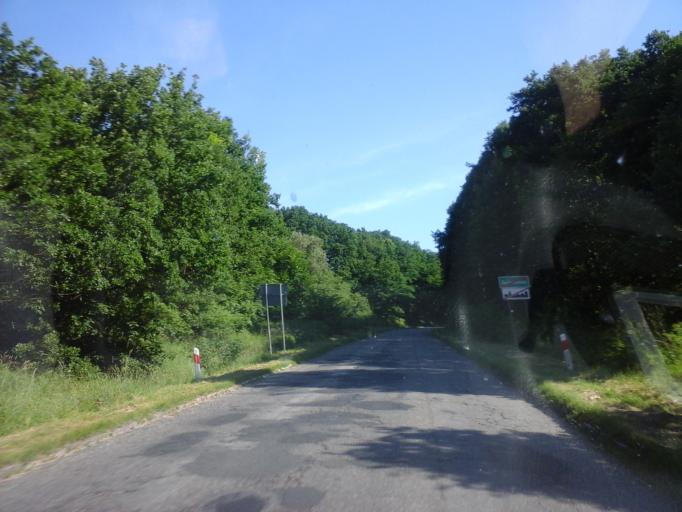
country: PL
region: West Pomeranian Voivodeship
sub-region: Powiat swidwinski
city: Polczyn-Zdroj
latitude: 53.6763
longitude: 16.0182
